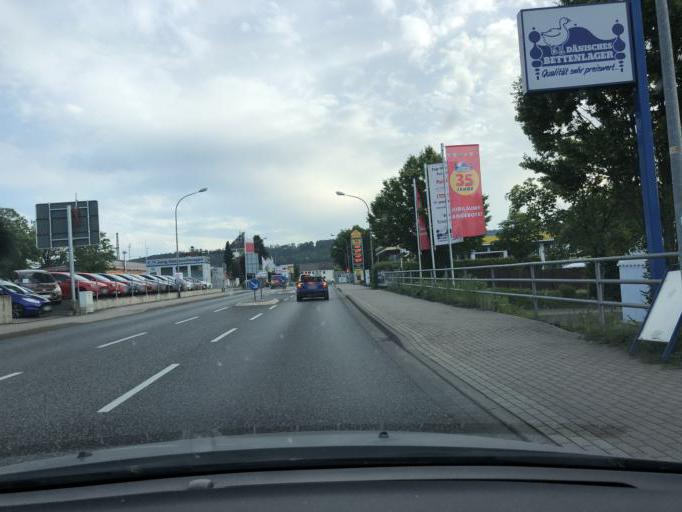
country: DE
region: Hesse
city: Melsungen
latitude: 51.1232
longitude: 9.5414
